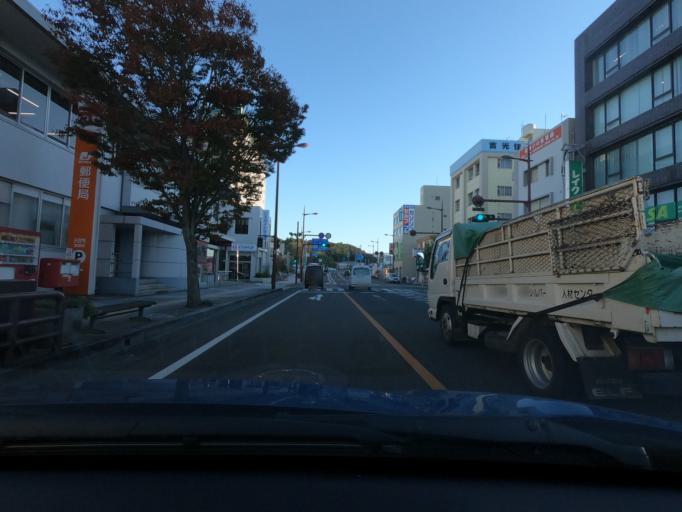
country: JP
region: Kagoshima
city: Satsumasendai
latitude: 31.8135
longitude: 130.3071
